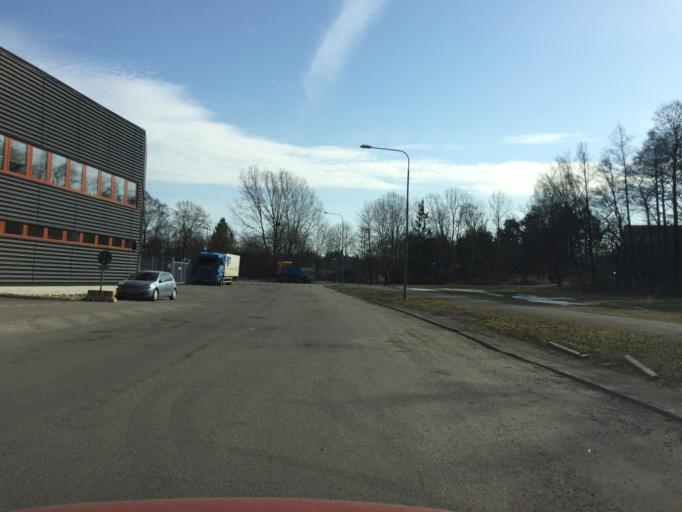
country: SE
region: Stockholm
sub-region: Stockholms Kommun
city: Arsta
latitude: 59.2899
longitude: 18.0079
